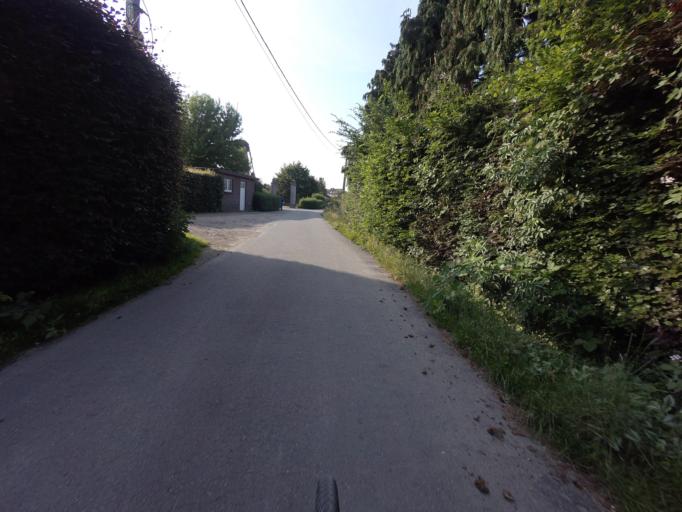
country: BE
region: Flanders
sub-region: Provincie Antwerpen
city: Schilde
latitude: 51.2096
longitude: 4.5966
